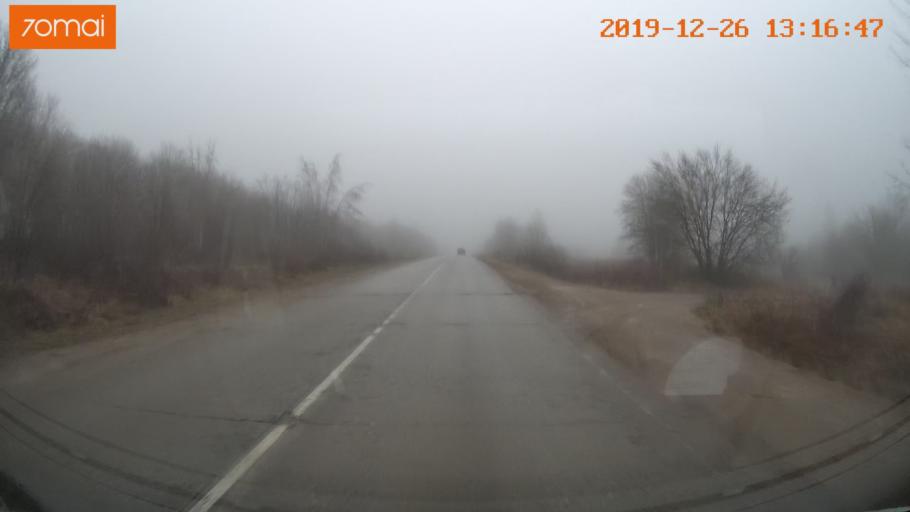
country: RU
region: Vologda
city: Cherepovets
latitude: 58.9774
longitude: 38.1091
